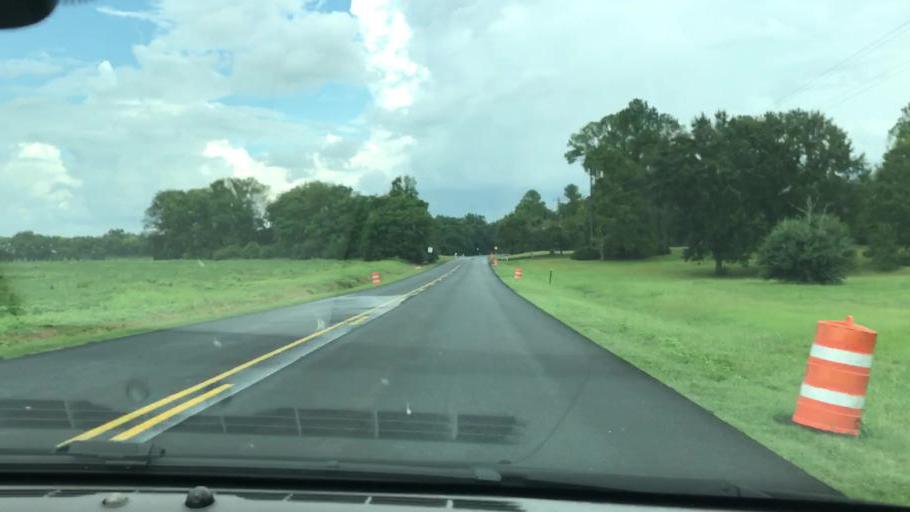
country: US
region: Georgia
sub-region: Early County
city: Blakely
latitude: 31.4038
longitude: -84.9604
